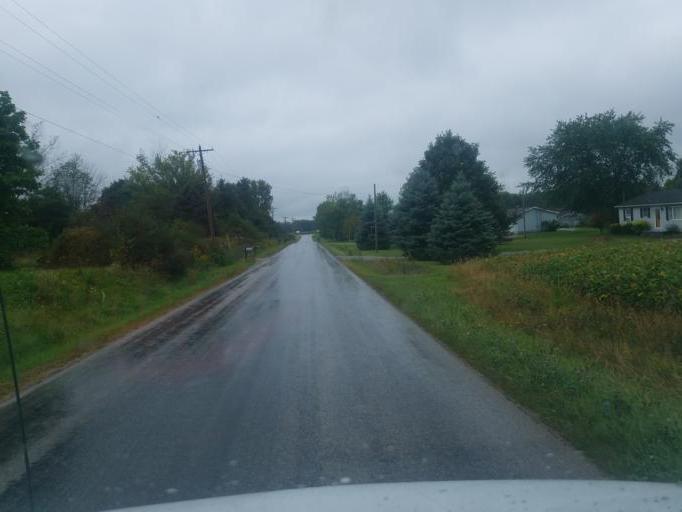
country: US
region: Ohio
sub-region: Wayne County
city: West Salem
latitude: 40.9377
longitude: -82.0780
